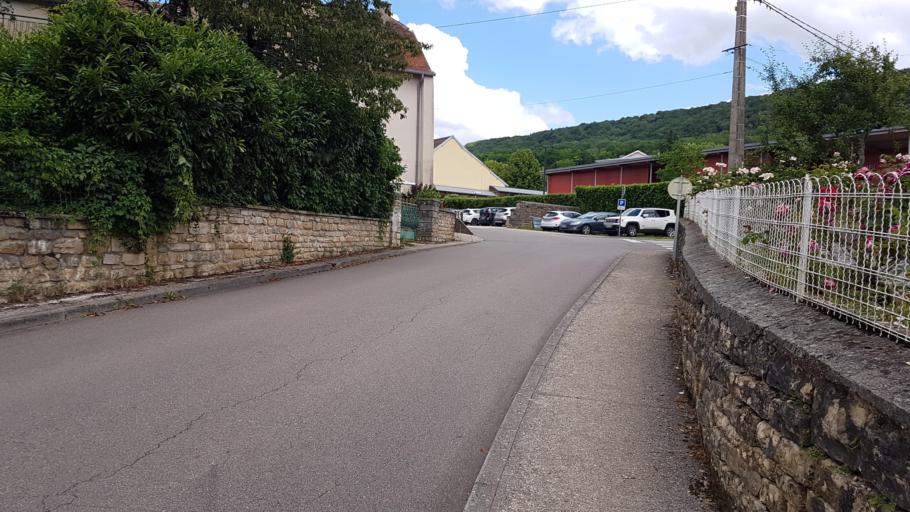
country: FR
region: Franche-Comte
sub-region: Departement du Jura
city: Perrigny
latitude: 46.6670
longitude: 5.5829
